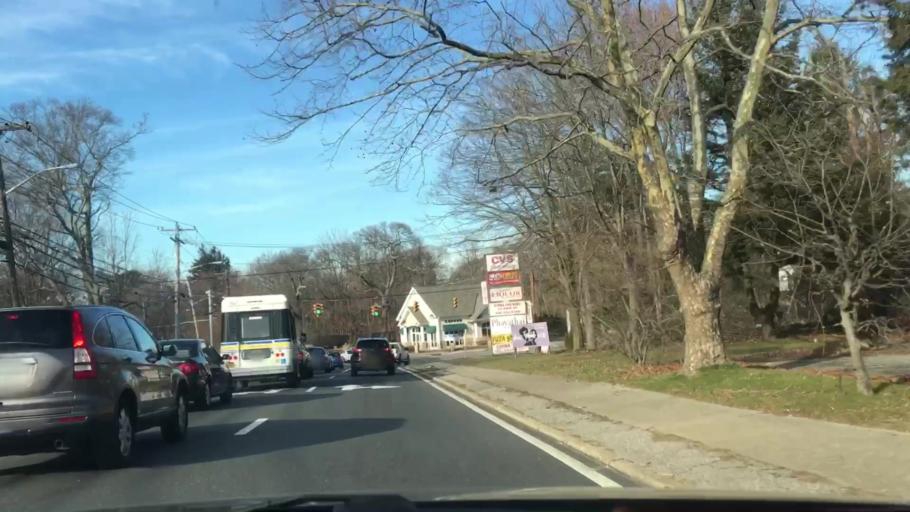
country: US
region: New York
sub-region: Suffolk County
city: Lake Grove
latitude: 40.8366
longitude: -73.1100
